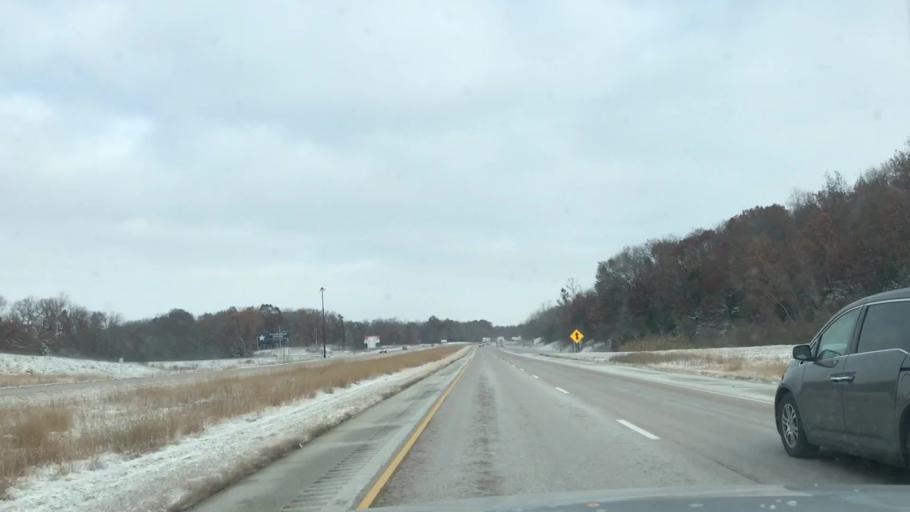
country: US
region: Illinois
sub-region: Macoupin County
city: Mount Olive
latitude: 39.0738
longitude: -89.7556
